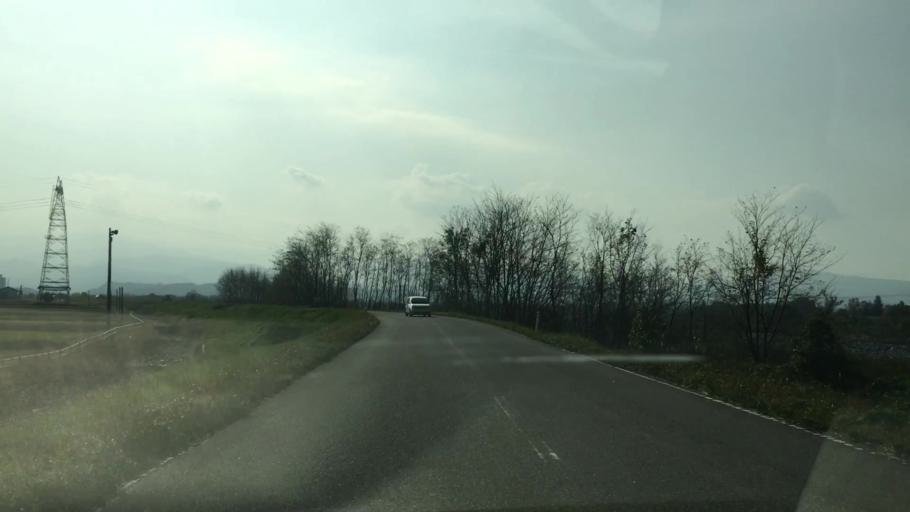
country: JP
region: Toyama
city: Toyama-shi
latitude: 36.6419
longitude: 137.2878
